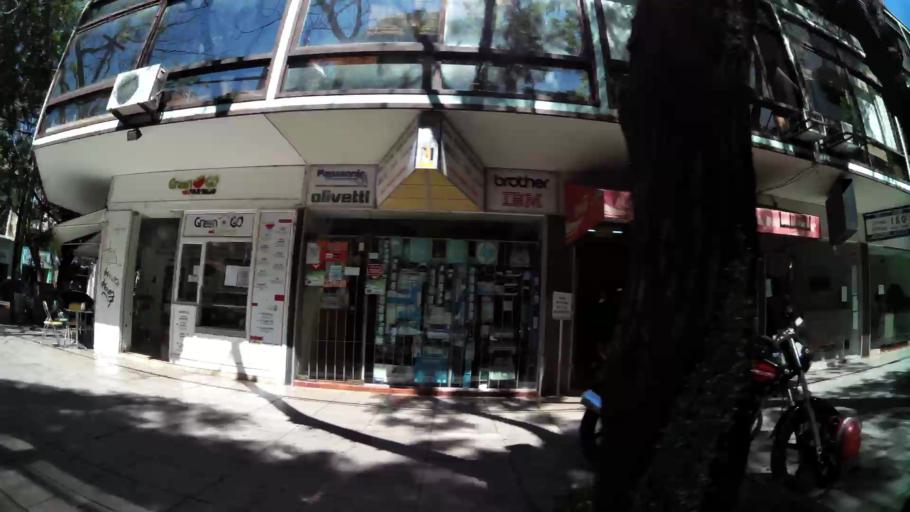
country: AR
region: Buenos Aires
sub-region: Partido de San Isidro
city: San Isidro
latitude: -34.4687
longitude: -58.5119
